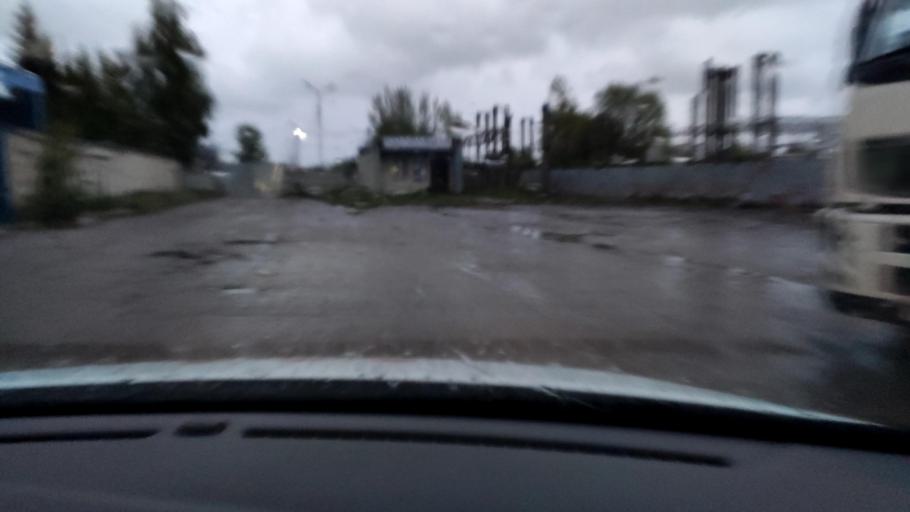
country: RU
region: Tatarstan
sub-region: Gorod Kazan'
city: Kazan
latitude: 55.7192
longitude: 49.1246
